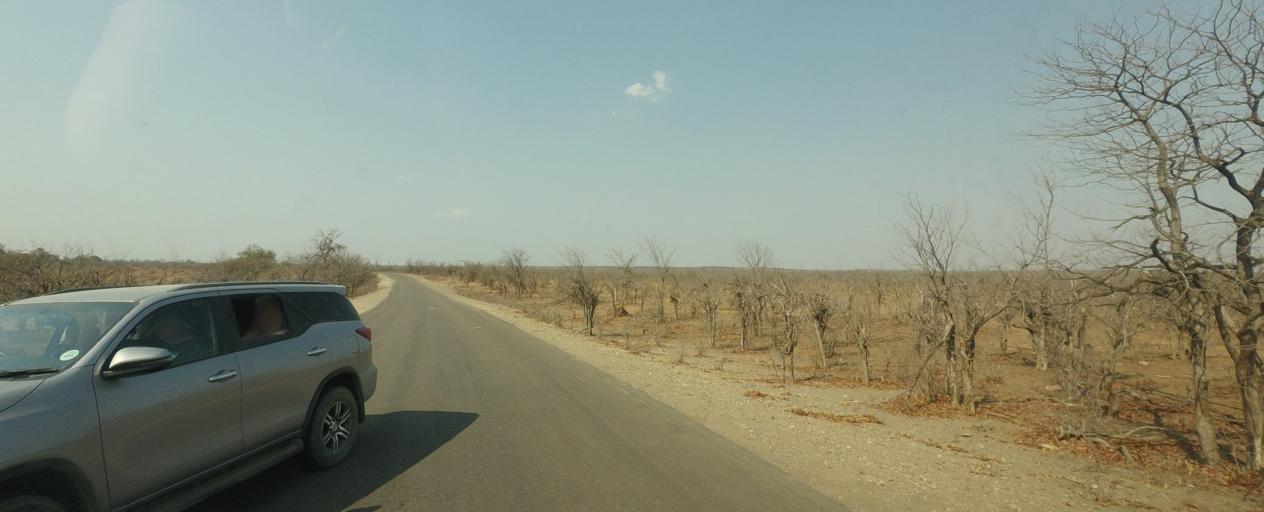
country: ZA
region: Limpopo
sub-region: Mopani District Municipality
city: Giyani
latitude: -23.1390
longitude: 31.3751
